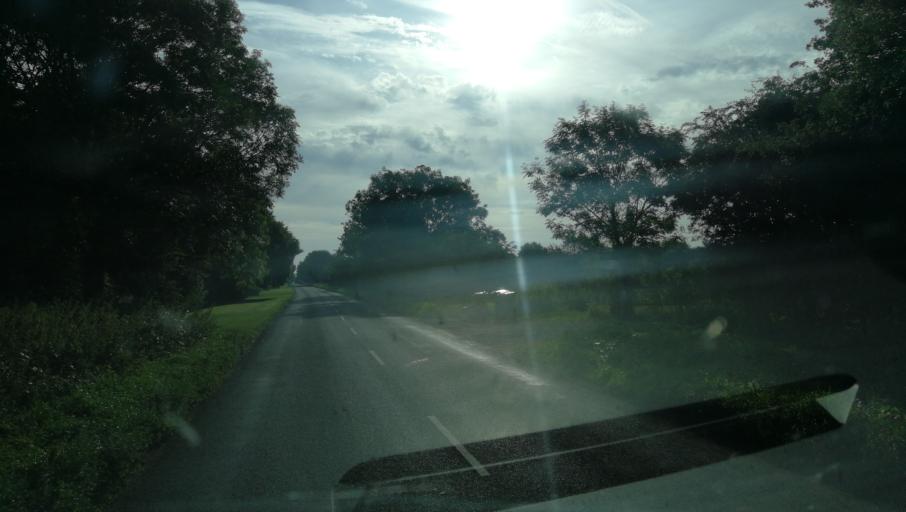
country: GB
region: England
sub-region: Oxfordshire
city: Adderbury
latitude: 52.0113
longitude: -1.3314
